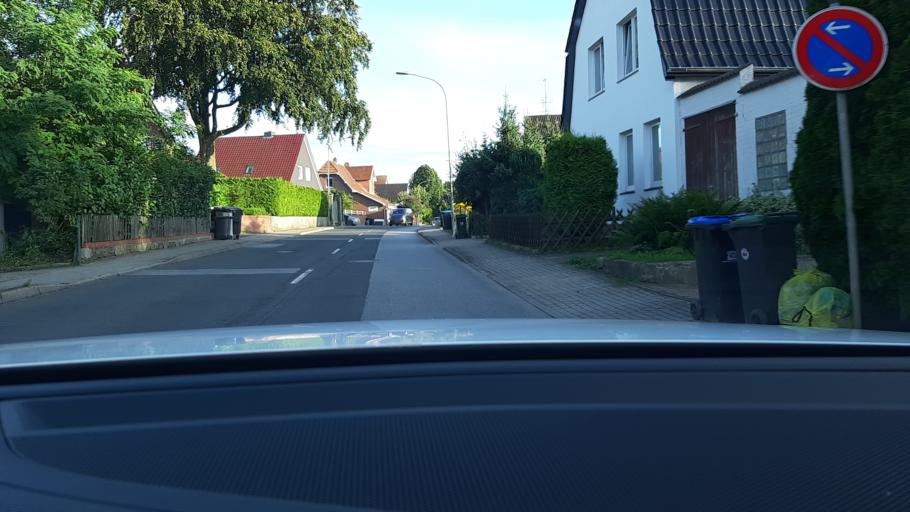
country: DE
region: Schleswig-Holstein
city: Stockelsdorf
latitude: 53.8998
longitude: 10.6455
